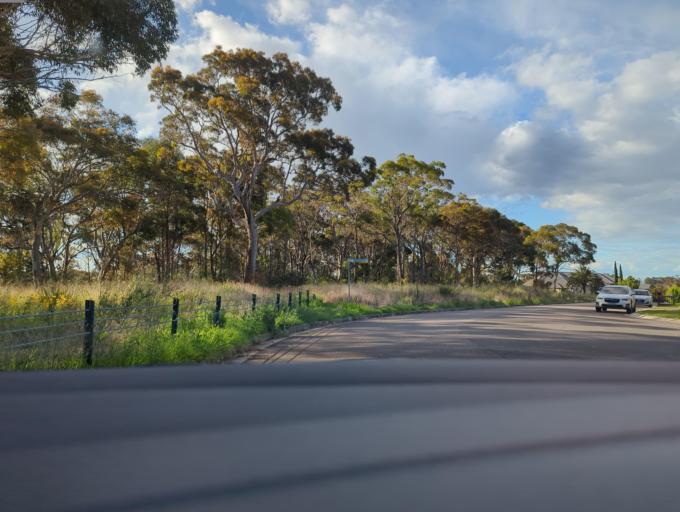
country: AU
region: New South Wales
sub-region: Sutherland Shire
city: Menai
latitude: -34.0279
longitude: 151.0027
